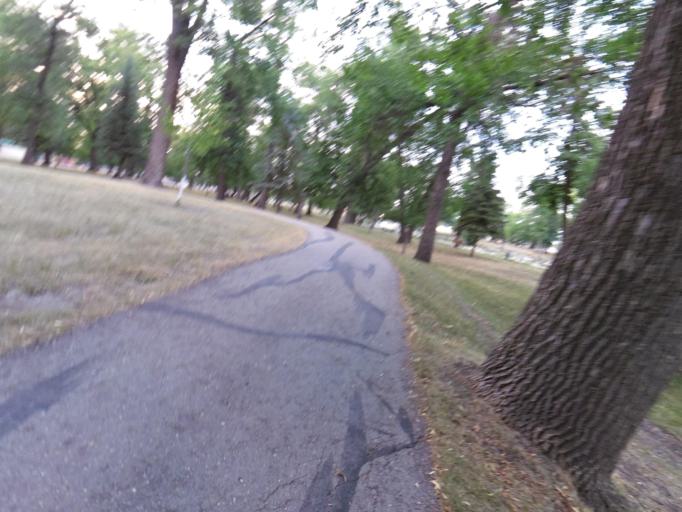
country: CA
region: Manitoba
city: Portage la Prairie
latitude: 49.9642
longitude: -98.2889
